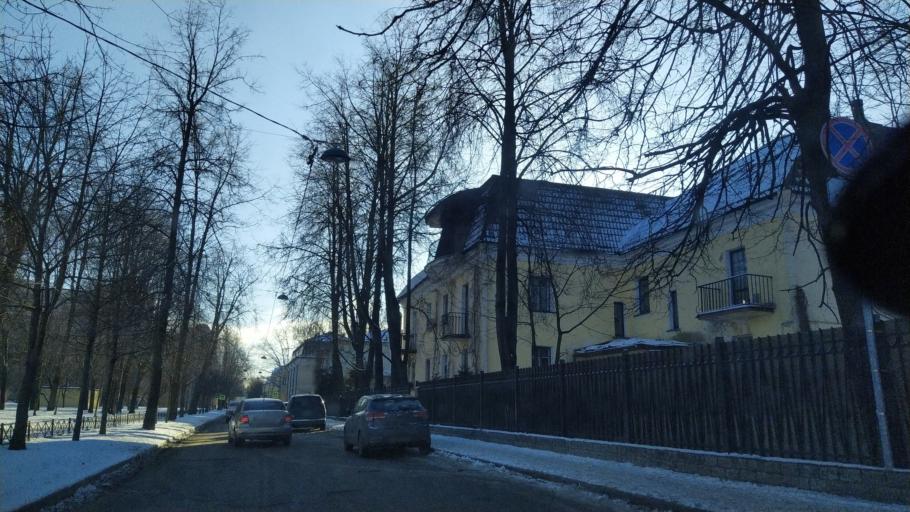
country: RU
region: St.-Petersburg
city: Novaya Derevnya
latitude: 59.9876
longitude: 30.2839
